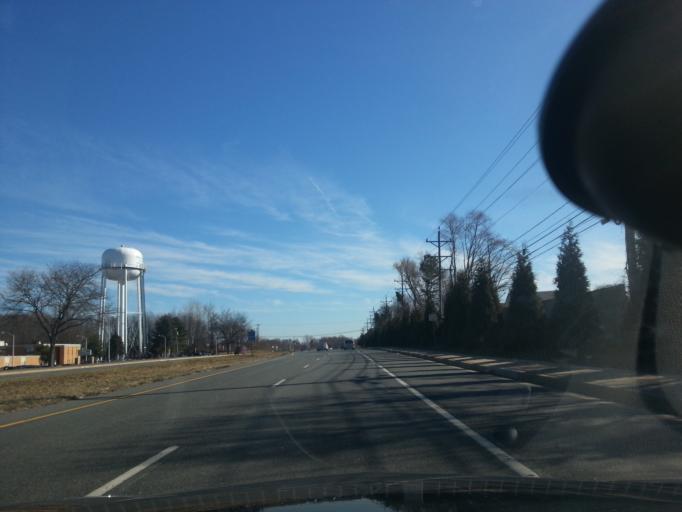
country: US
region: Delaware
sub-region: New Castle County
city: Brookside
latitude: 39.6712
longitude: -75.7093
